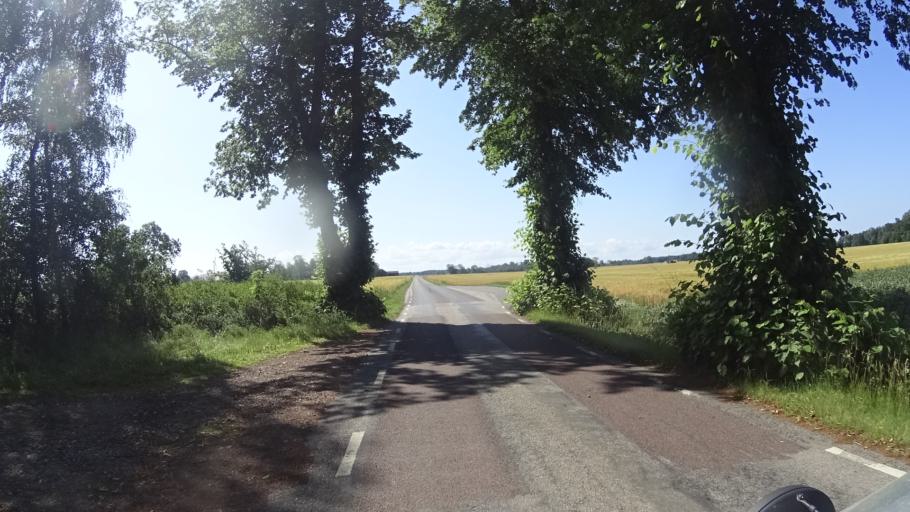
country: SE
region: OEstergoetland
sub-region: Vadstena Kommun
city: Herrestad
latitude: 58.3170
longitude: 14.8427
